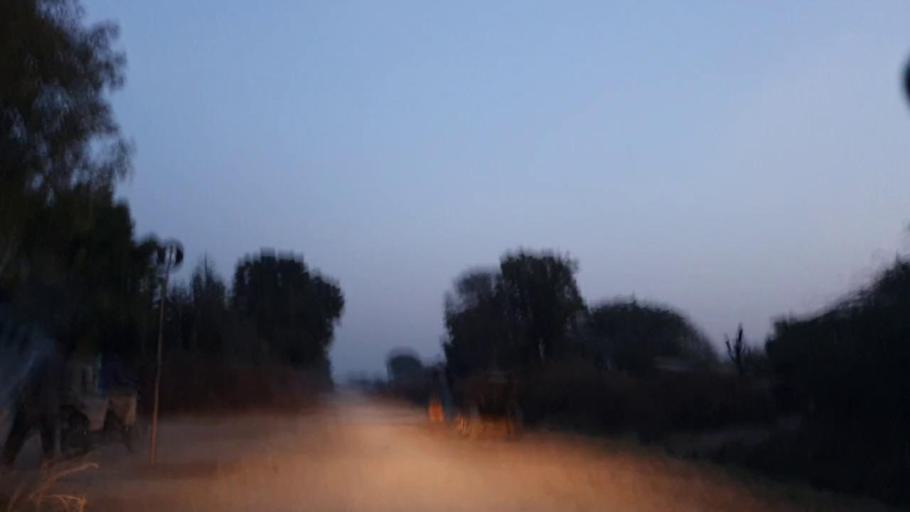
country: PK
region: Sindh
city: Tando Ghulam Ali
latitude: 25.1077
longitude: 68.9079
